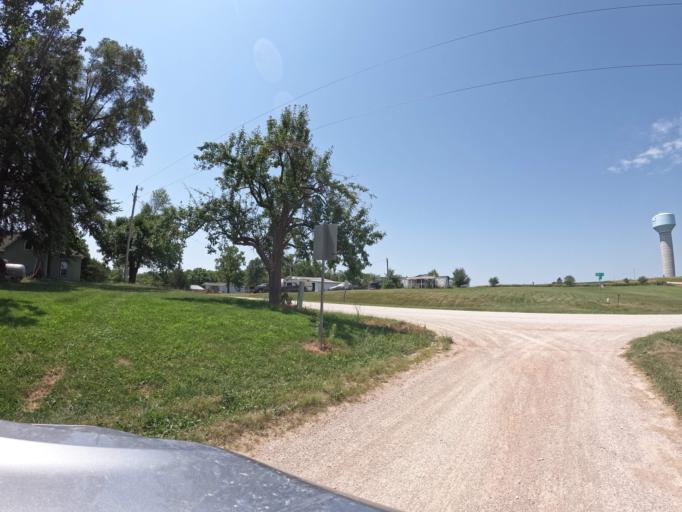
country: US
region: Iowa
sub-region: Appanoose County
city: Centerville
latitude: 40.7864
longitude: -92.9062
